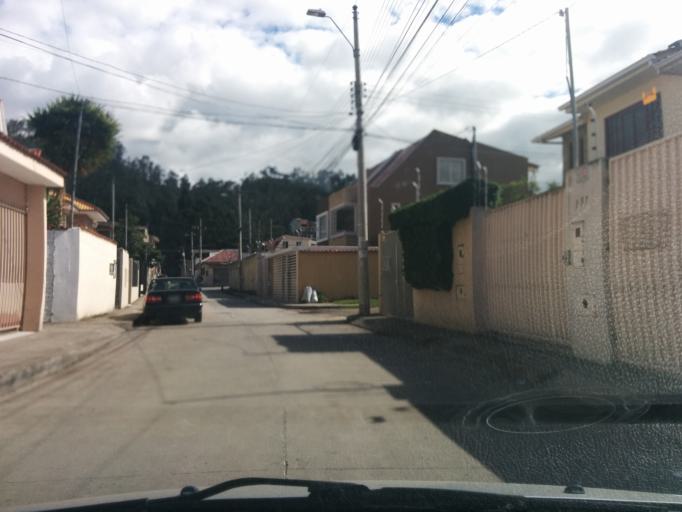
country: EC
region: Azuay
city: Cuenca
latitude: -2.9150
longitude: -79.0123
